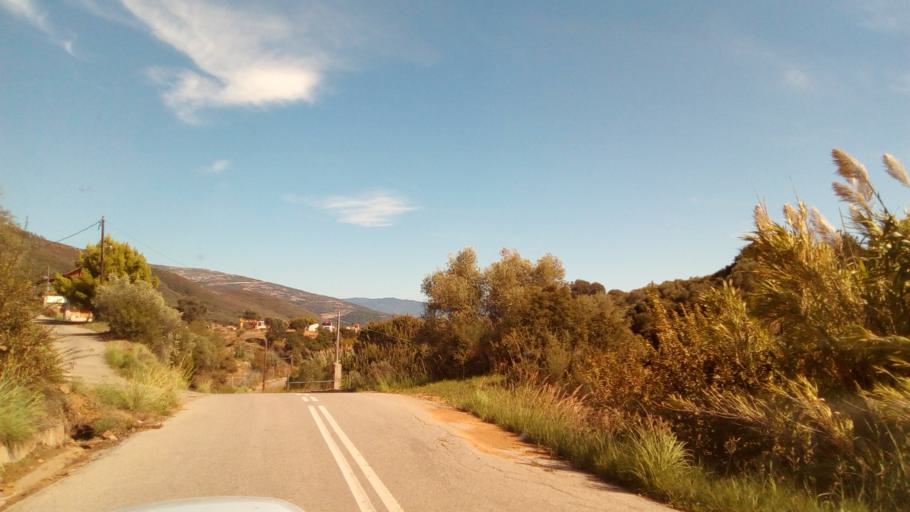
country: GR
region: West Greece
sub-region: Nomos Aitolias kai Akarnanias
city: Antirrio
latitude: 38.3679
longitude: 21.7691
